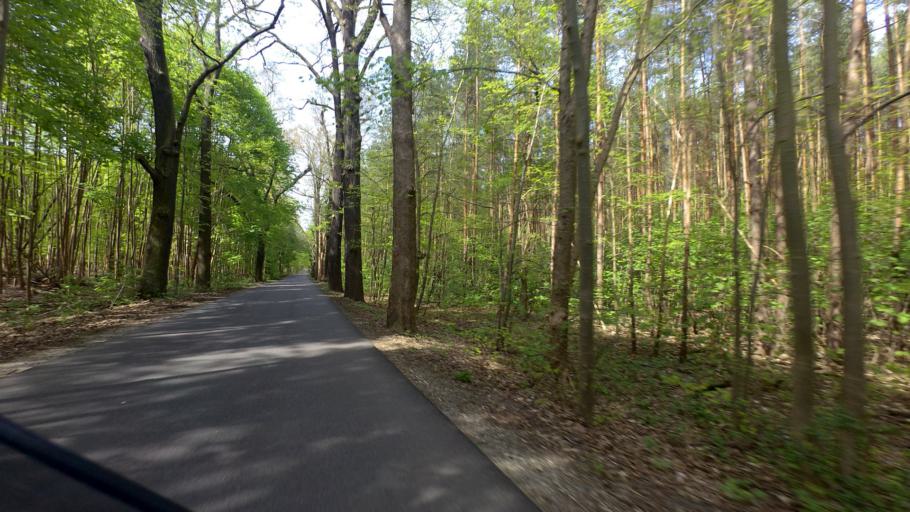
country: DE
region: Brandenburg
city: Potsdam
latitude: 52.4359
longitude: 13.0806
